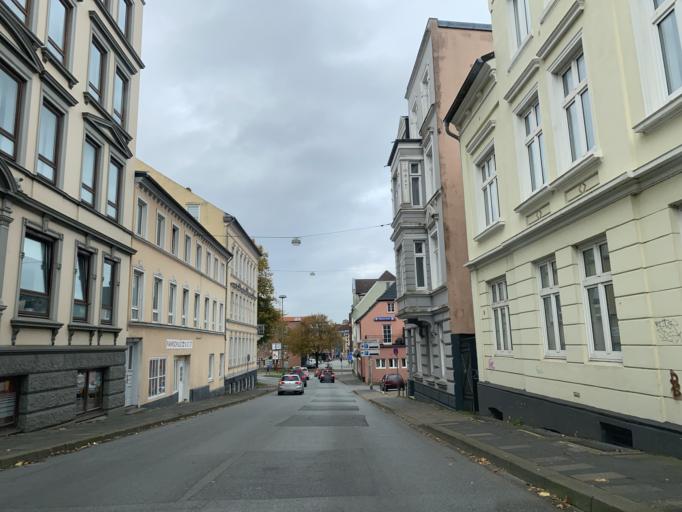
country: DE
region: Schleswig-Holstein
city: Flensburg
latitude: 54.7793
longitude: 9.4354
